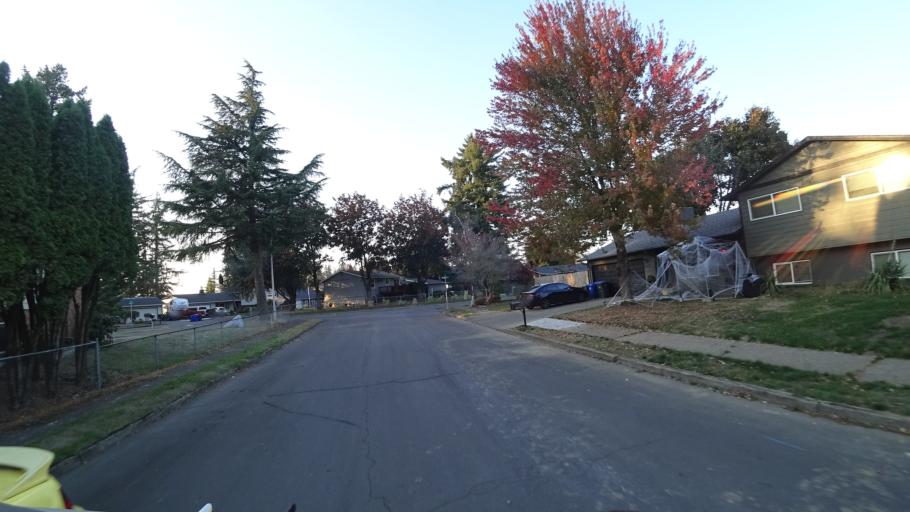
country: US
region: Oregon
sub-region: Multnomah County
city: Fairview
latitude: 45.5175
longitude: -122.4517
